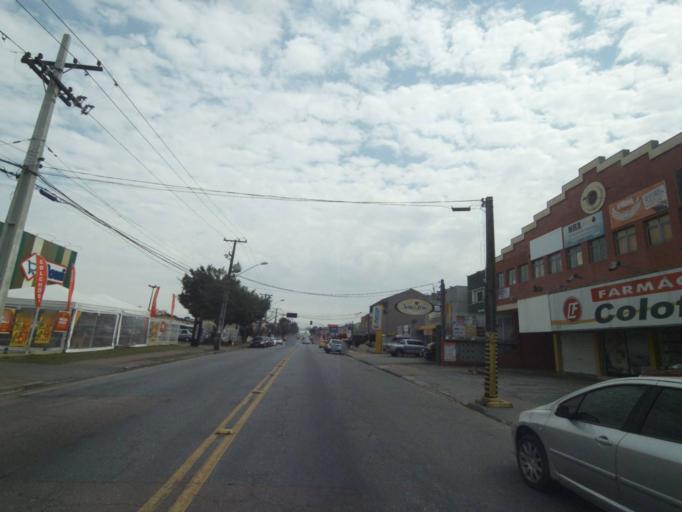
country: BR
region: Parana
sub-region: Pinhais
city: Pinhais
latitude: -25.4011
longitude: -49.2065
